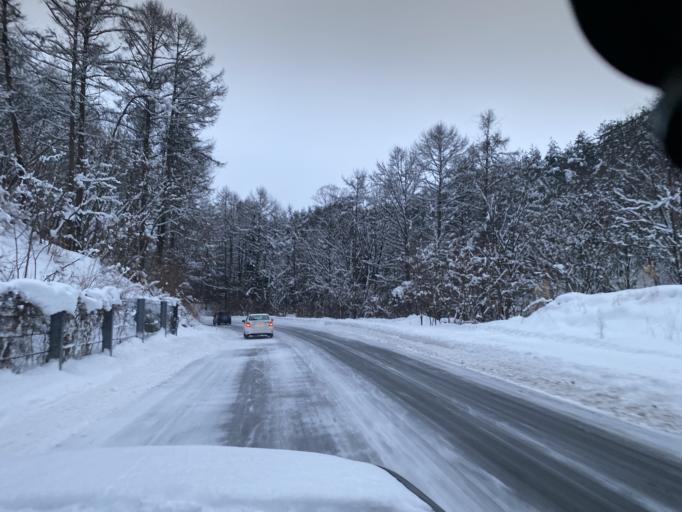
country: JP
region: Nagano
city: Omachi
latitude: 36.5324
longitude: 137.8648
